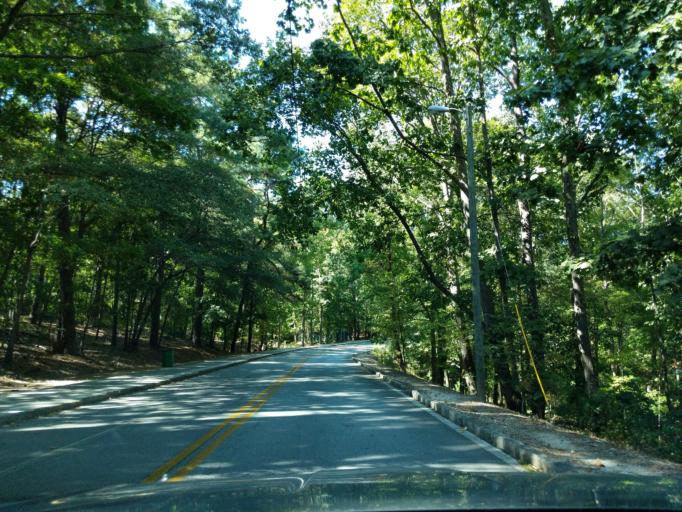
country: US
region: Georgia
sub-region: DeKalb County
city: Stone Mountain
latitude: 33.7997
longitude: -84.1348
